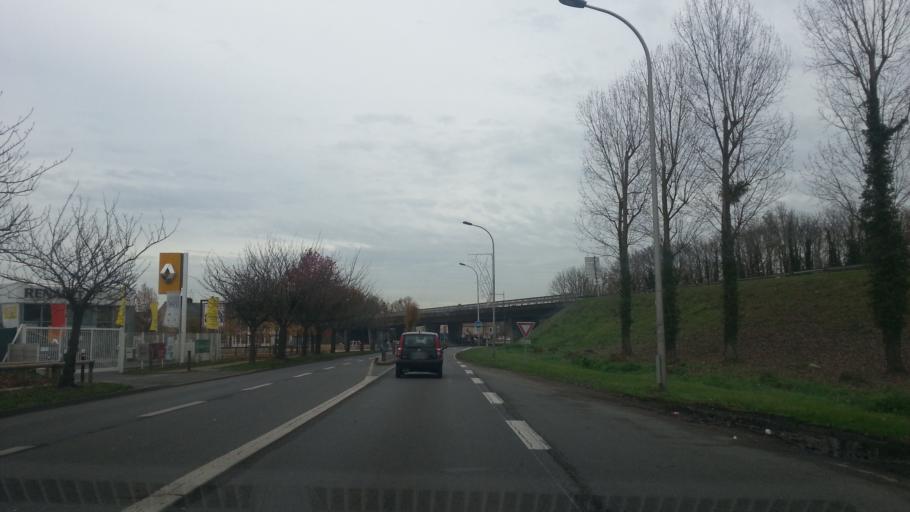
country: FR
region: Picardie
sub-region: Departement de l'Oise
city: Montataire
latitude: 49.2541
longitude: 2.4443
